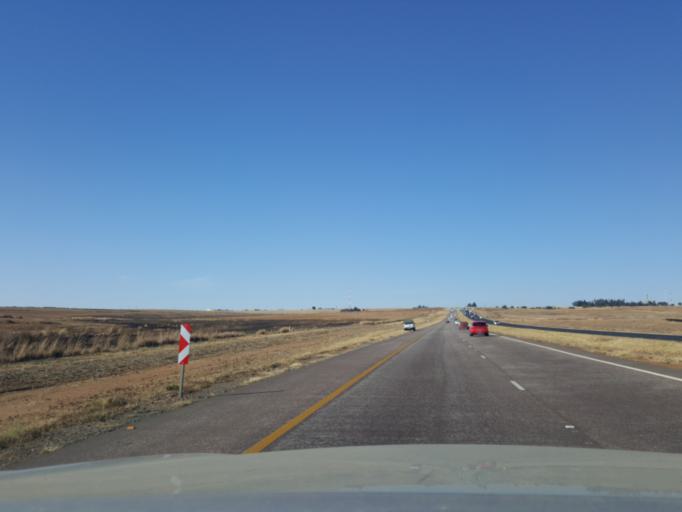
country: ZA
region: Mpumalanga
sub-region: Nkangala District Municipality
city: Belfast
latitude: -25.8251
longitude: 29.8363
